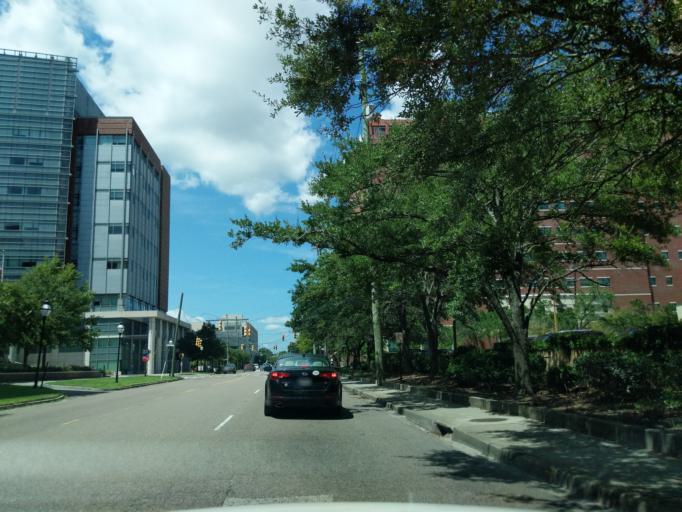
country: US
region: South Carolina
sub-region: Charleston County
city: Charleston
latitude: 32.7834
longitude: -79.9509
